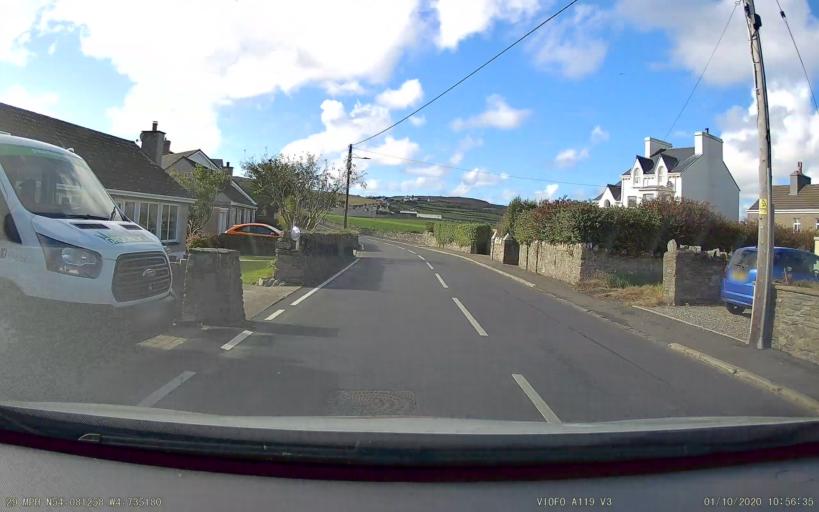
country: IM
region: Port Erin
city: Port Erin
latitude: 54.0813
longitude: -4.7353
